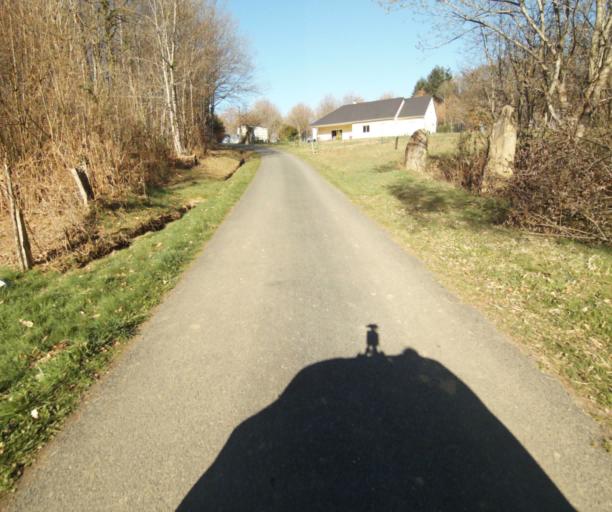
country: FR
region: Limousin
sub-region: Departement de la Correze
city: Saint-Clement
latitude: 45.3710
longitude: 1.6501
